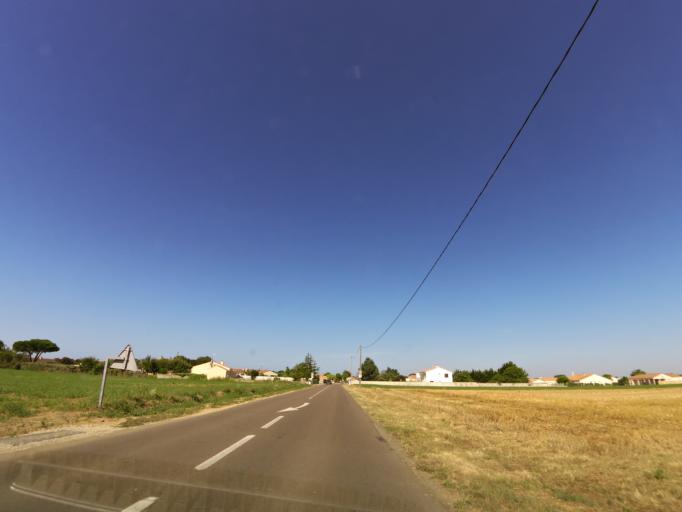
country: FR
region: Pays de la Loire
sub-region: Departement de la Vendee
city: Jard-sur-Mer
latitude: 46.4197
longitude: -1.5600
